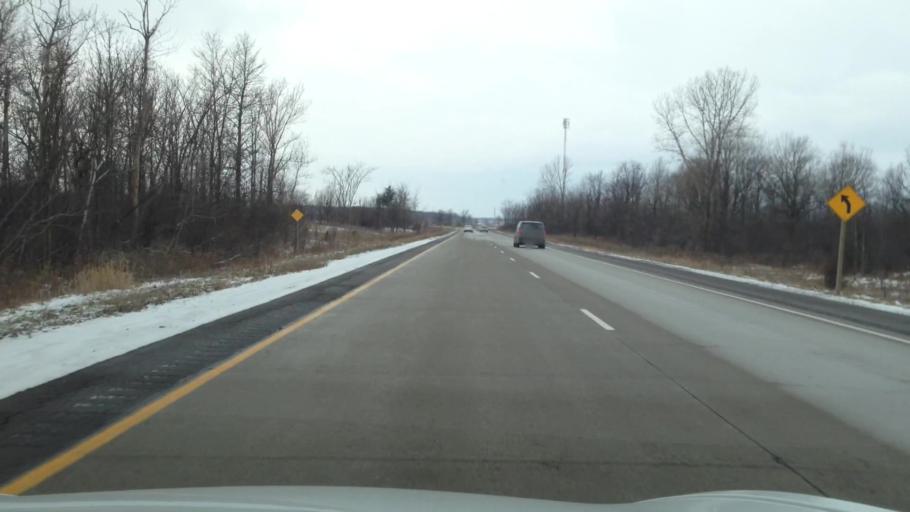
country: CA
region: Ontario
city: Casselman
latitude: 45.3809
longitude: -74.8169
